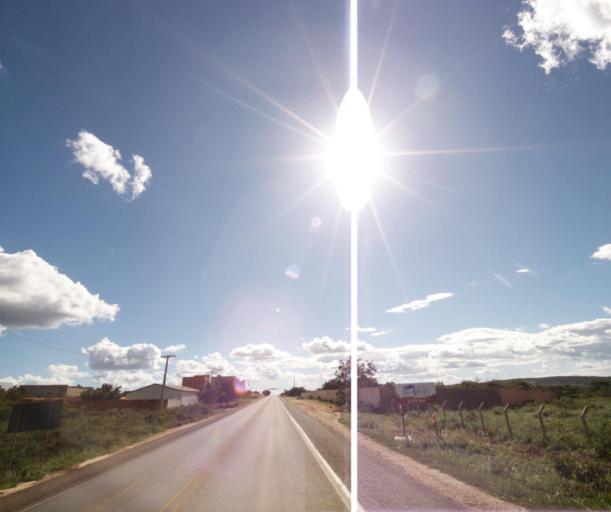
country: BR
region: Bahia
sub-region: Caetite
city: Caetite
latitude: -14.0647
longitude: -42.5247
